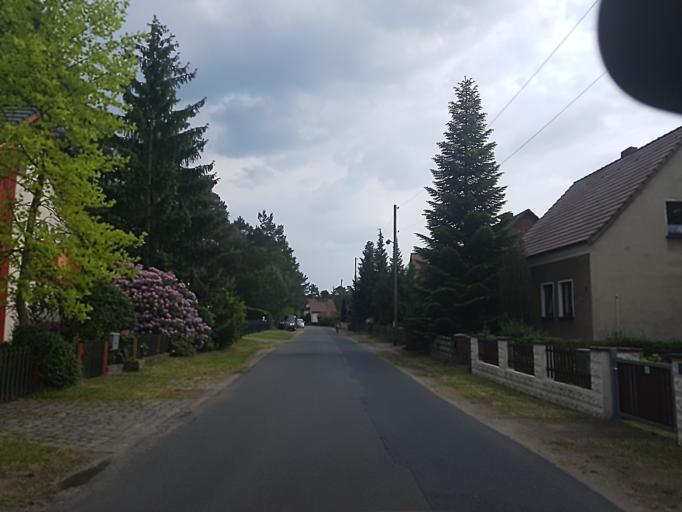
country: DE
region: Saxony-Anhalt
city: Muhlanger
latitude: 51.8589
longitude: 12.7248
